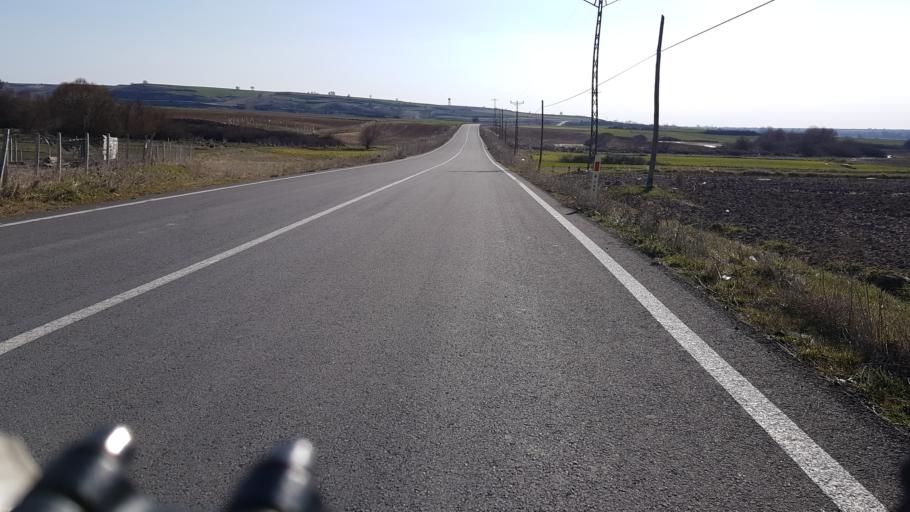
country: TR
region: Tekirdag
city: Saray
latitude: 41.3655
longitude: 27.8584
